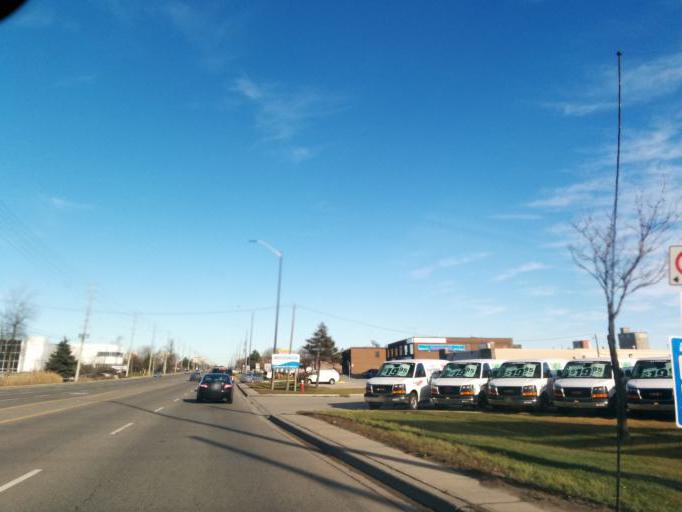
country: CA
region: Ontario
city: Oakville
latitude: 43.4968
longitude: -79.6454
